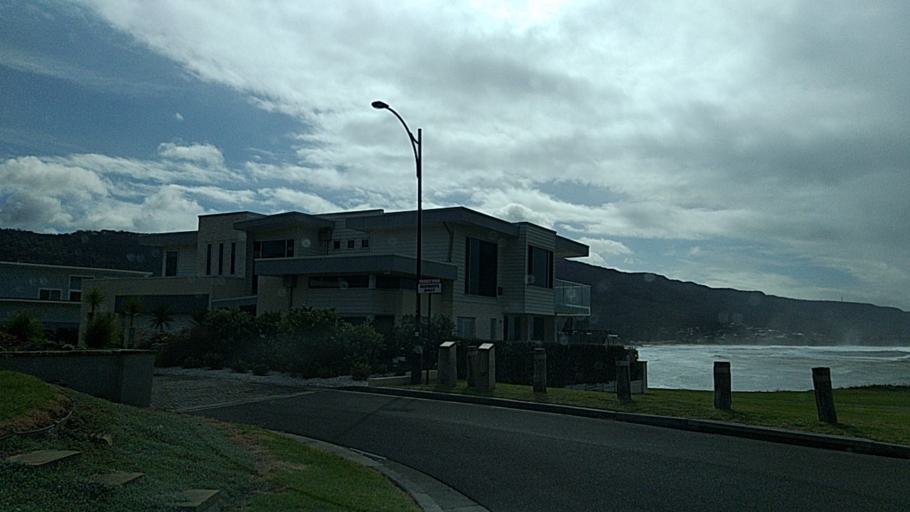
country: AU
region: New South Wales
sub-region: Wollongong
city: Bulli
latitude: -34.3297
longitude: 150.9252
